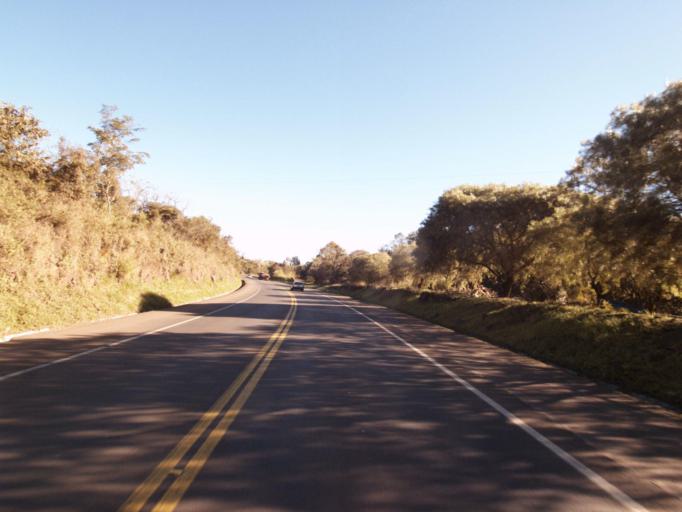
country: BR
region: Santa Catarina
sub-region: Chapeco
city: Chapeco
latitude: -26.9668
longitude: -52.5706
